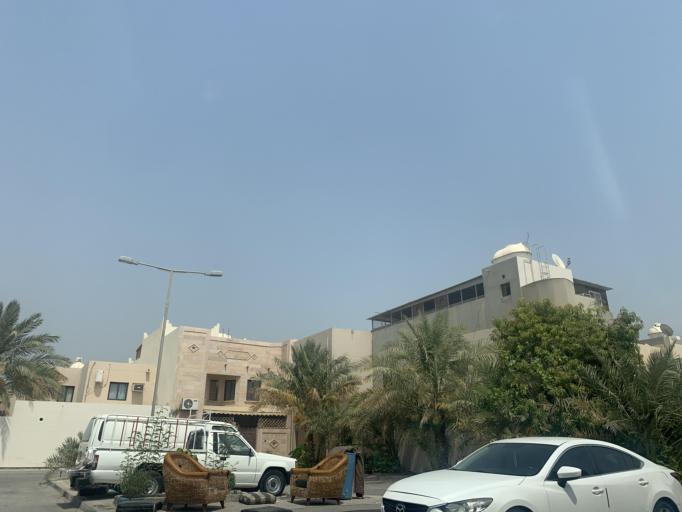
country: BH
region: Manama
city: Jidd Hafs
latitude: 26.2099
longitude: 50.5072
